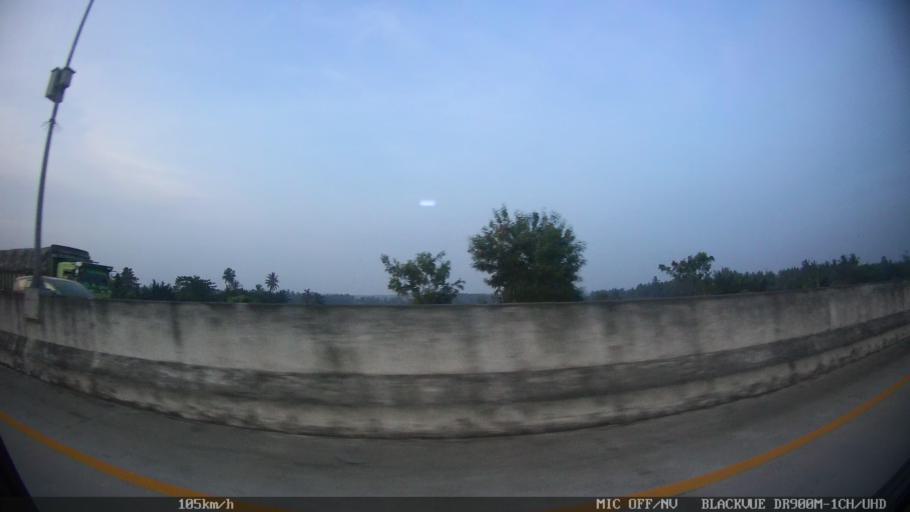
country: ID
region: Lampung
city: Pasuruan
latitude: -5.7151
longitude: 105.6551
